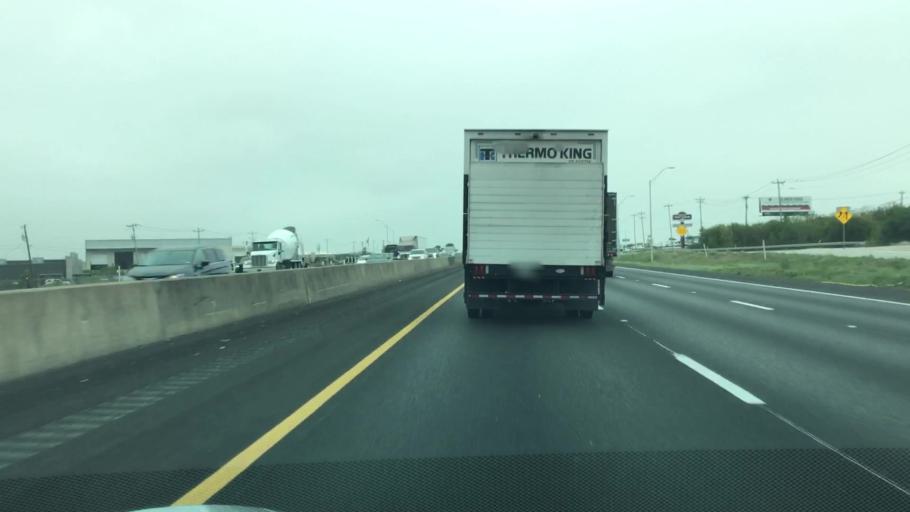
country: US
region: Texas
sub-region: Hays County
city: Buda
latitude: 30.0535
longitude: -97.8367
